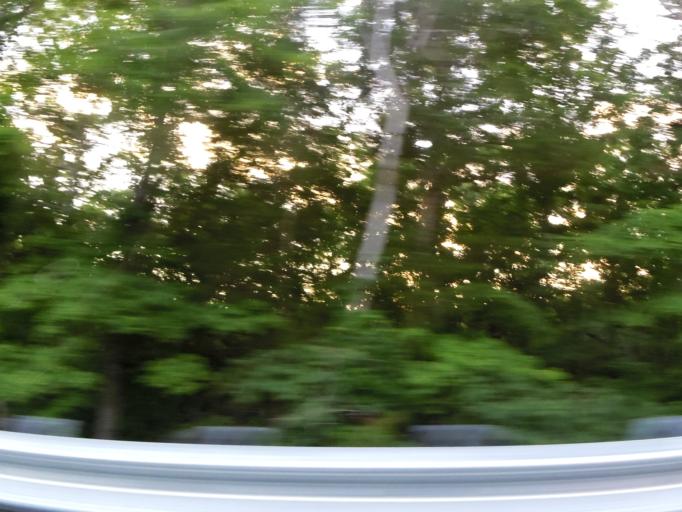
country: US
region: Missouri
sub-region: Jefferson County
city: Cedar Hill
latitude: 38.3147
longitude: -90.6483
